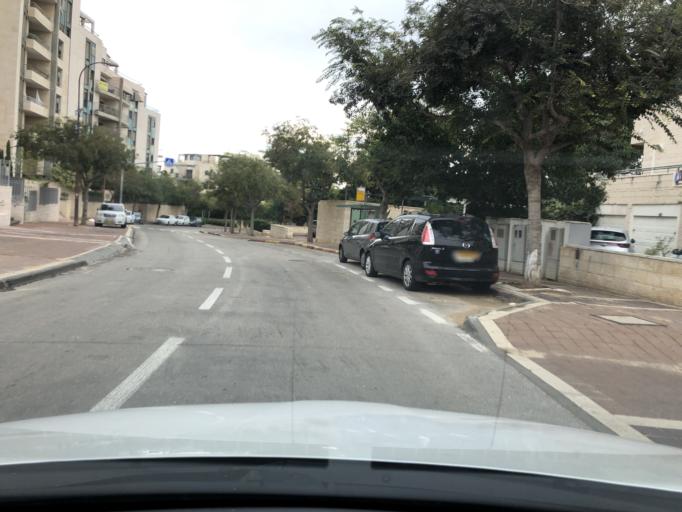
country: IL
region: Central District
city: Modiin
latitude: 31.9070
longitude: 35.0104
